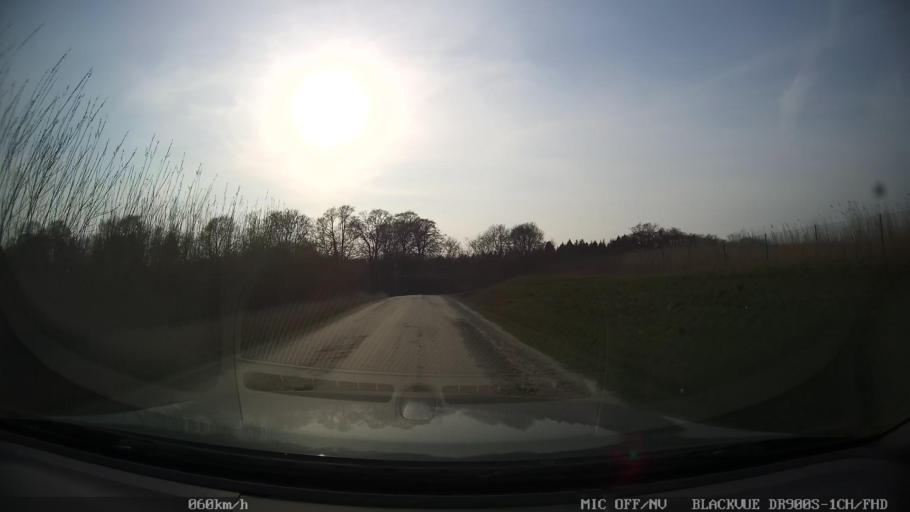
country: SE
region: Skane
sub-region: Ystads Kommun
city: Ystad
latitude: 55.4597
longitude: 13.7844
